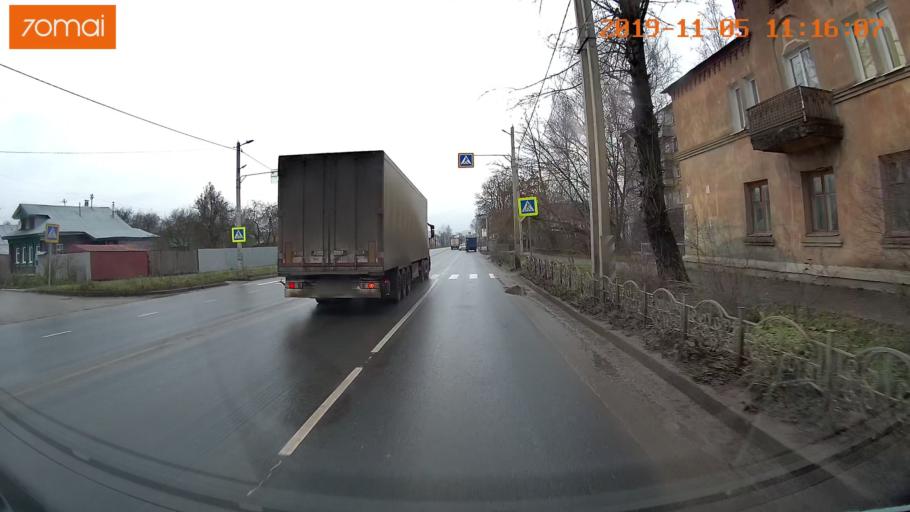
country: RU
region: Ivanovo
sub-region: Gorod Ivanovo
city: Ivanovo
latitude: 56.9820
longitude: 40.9537
